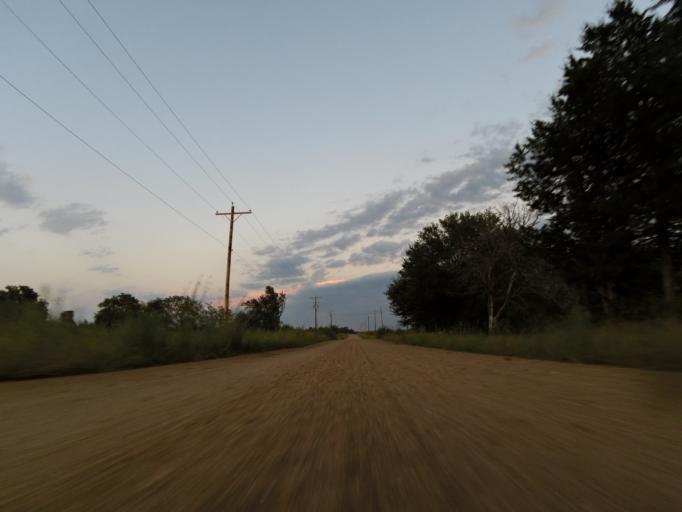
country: US
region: Kansas
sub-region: Reno County
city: South Hutchinson
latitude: 37.9555
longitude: -98.0424
